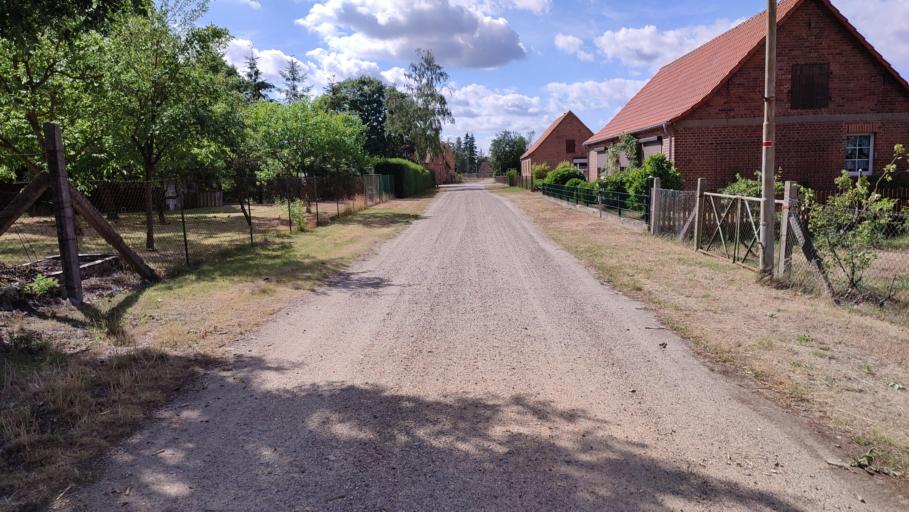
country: DE
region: Lower Saxony
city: Damnatz
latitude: 53.1714
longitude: 11.1725
